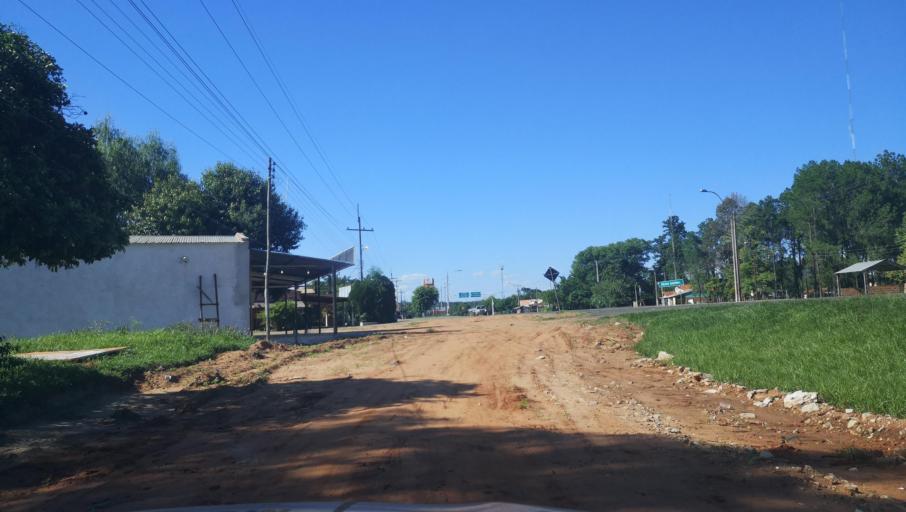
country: PY
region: Caaguazu
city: Carayao
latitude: -25.2003
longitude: -56.3982
